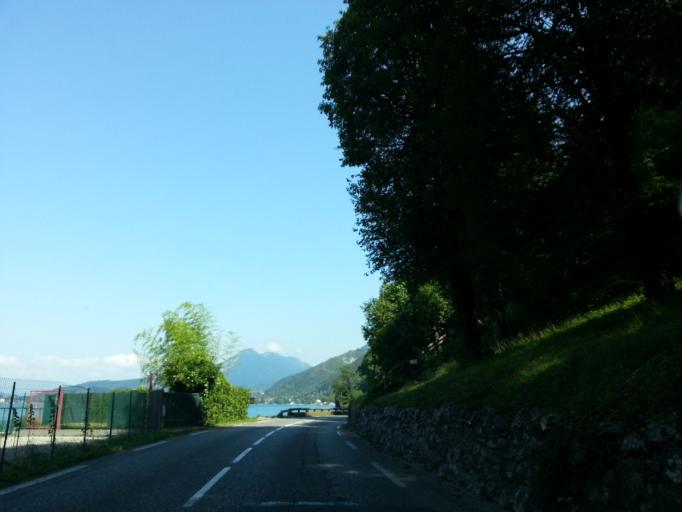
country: FR
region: Rhone-Alpes
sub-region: Departement de la Haute-Savoie
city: Doussard
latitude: 45.8063
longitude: 6.2322
